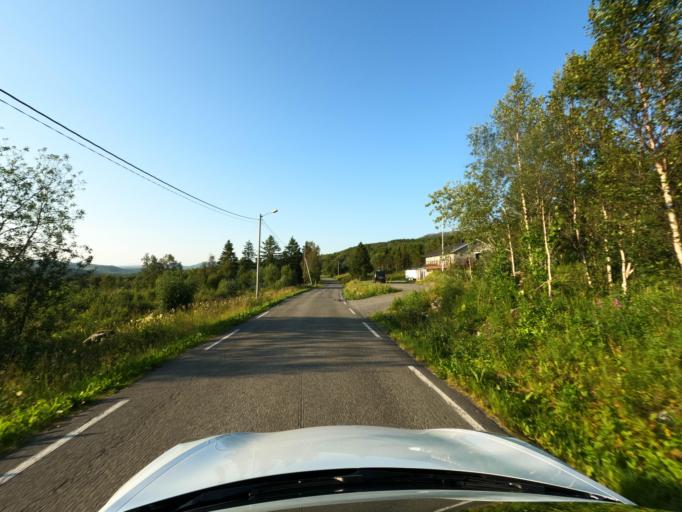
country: NO
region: Nordland
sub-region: Ballangen
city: Ballangen
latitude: 68.4962
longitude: 16.7354
